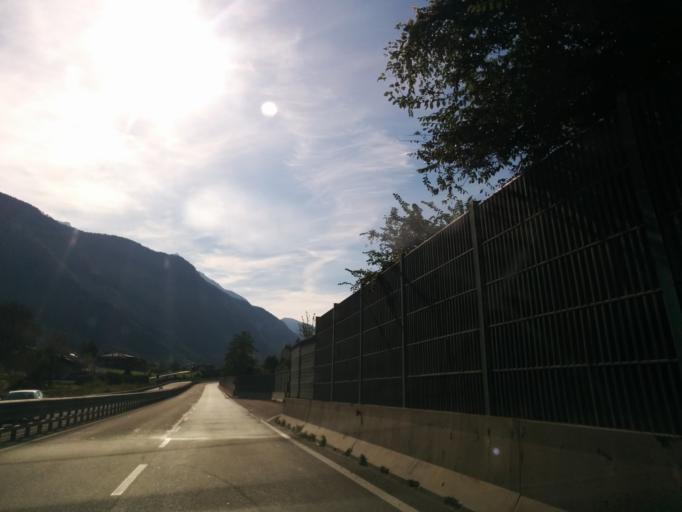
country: IT
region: Trentino-Alto Adige
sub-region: Provincia di Trento
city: Roncegno
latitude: 46.0319
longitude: 11.3919
